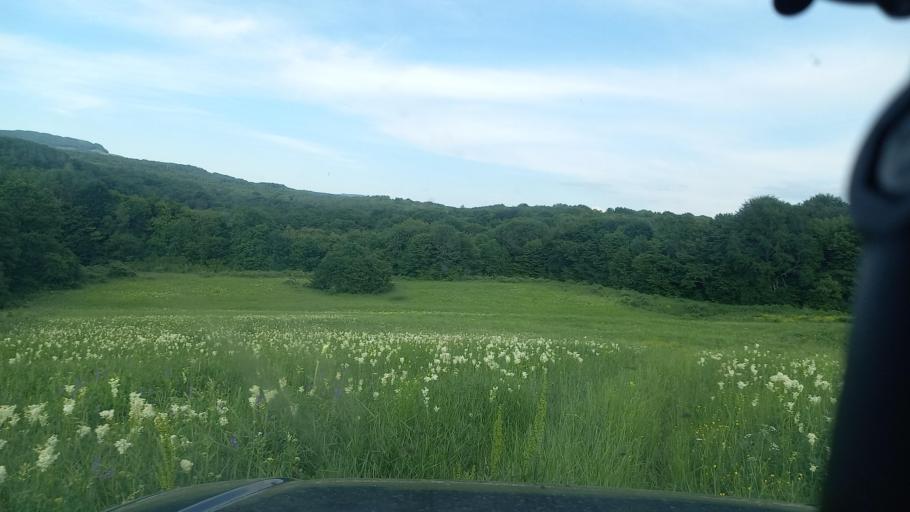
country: RU
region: Karachayevo-Cherkesiya
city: Pregradnaya
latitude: 44.1320
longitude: 41.0963
